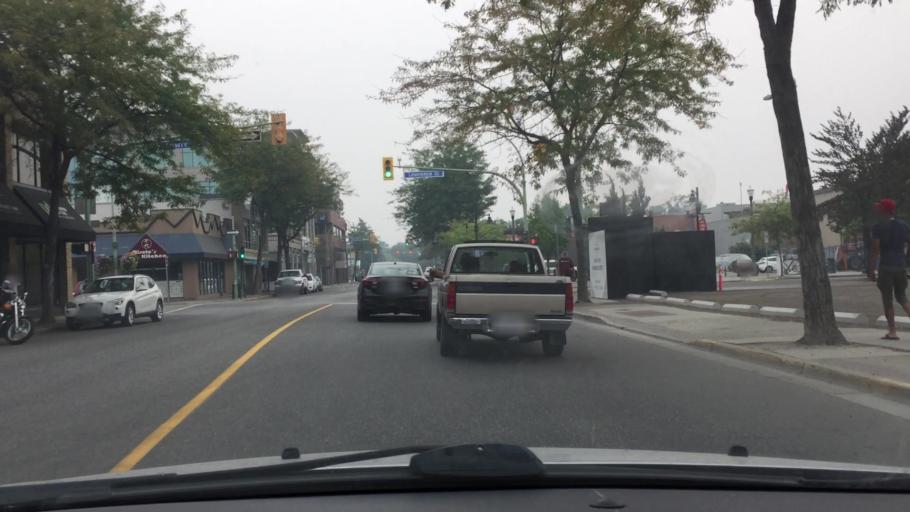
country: CA
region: British Columbia
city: Kelowna
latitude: 49.8857
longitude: -119.4936
